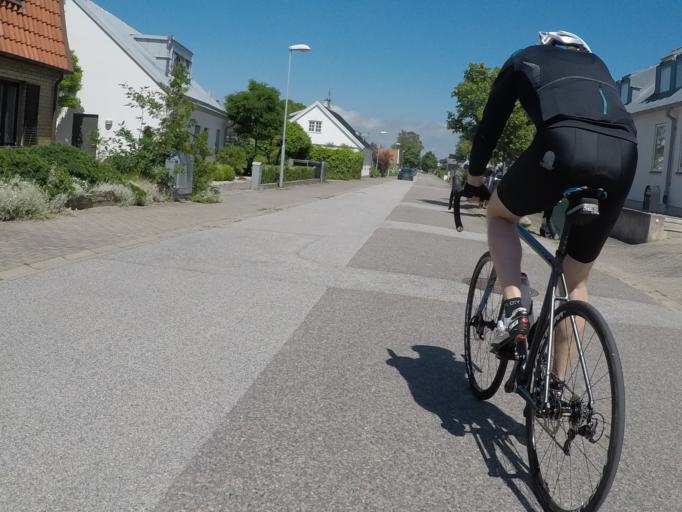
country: SE
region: Skane
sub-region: Lomma Kommun
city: Lomma
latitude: 55.6618
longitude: 13.0613
